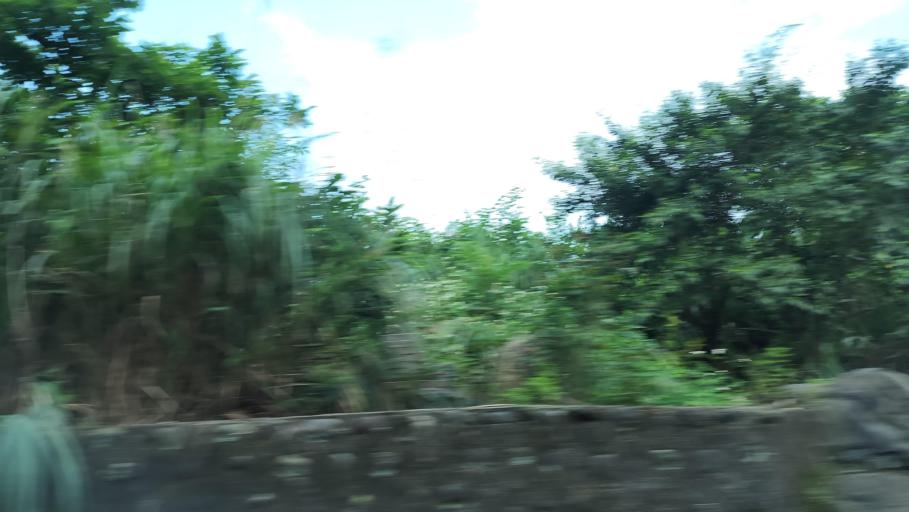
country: TW
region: Taiwan
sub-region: Keelung
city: Keelung
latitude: 25.1921
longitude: 121.6432
